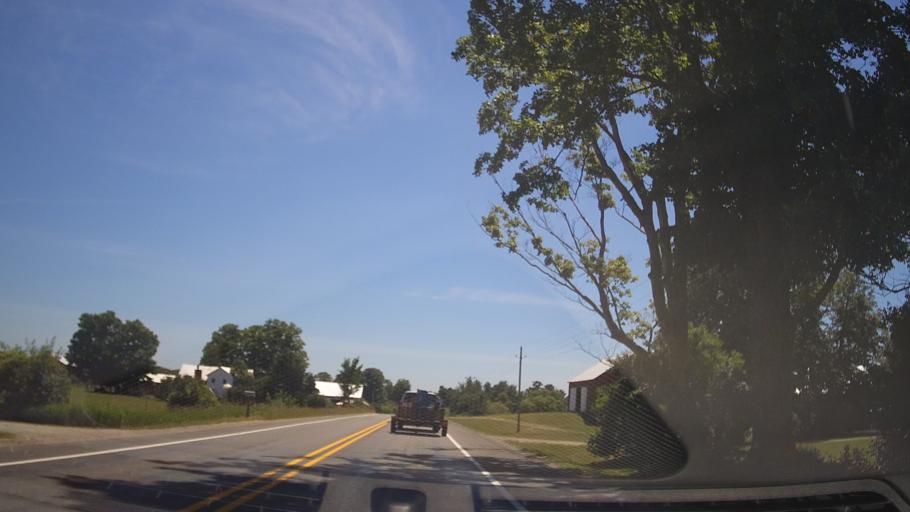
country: US
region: Michigan
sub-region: Grand Traverse County
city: Kingsley
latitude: 44.6078
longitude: -85.6965
